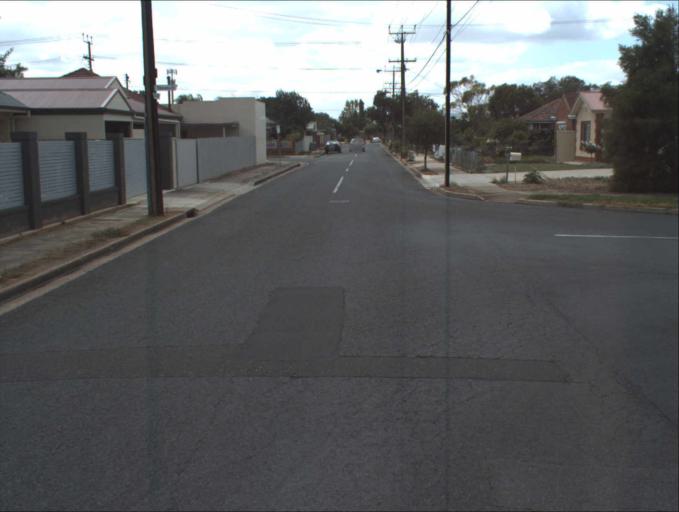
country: AU
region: South Australia
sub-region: Charles Sturt
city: Woodville
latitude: -34.8793
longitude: 138.5612
